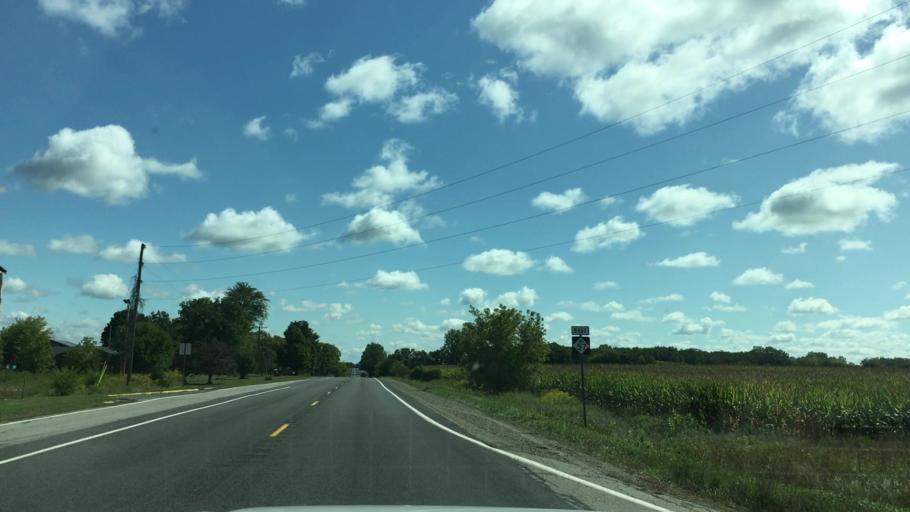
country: US
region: Michigan
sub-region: Montcalm County
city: Carson City
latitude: 43.1774
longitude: -84.9155
